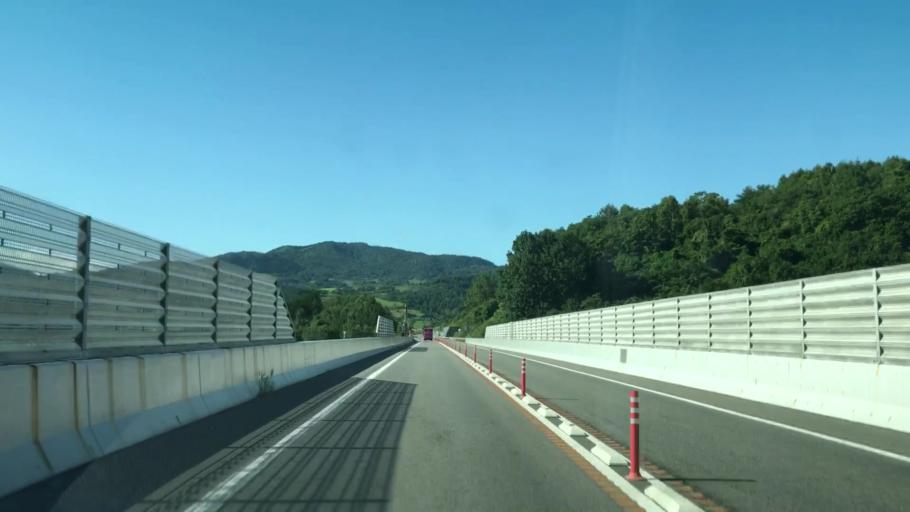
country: JP
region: Hokkaido
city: Date
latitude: 42.5384
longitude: 140.7969
